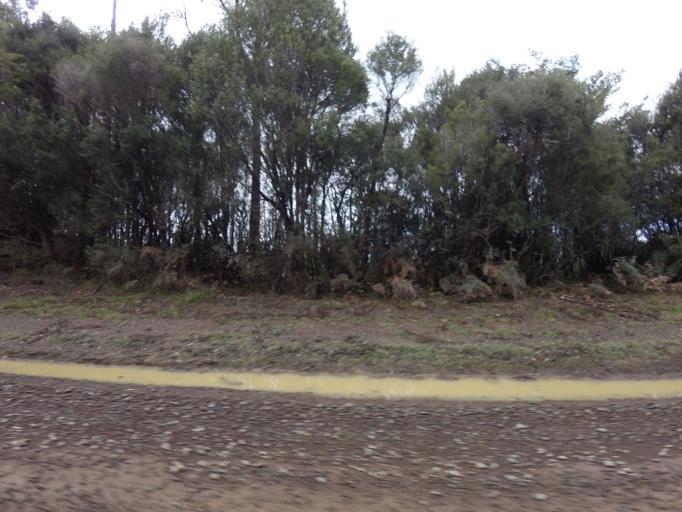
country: AU
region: Tasmania
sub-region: Huon Valley
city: Geeveston
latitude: -43.5428
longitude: 146.8913
